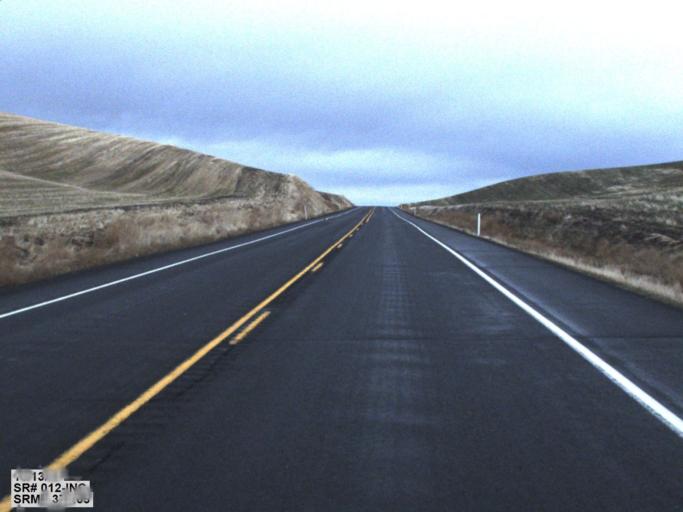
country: US
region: Washington
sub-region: Columbia County
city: Dayton
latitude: 46.3688
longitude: -117.9466
